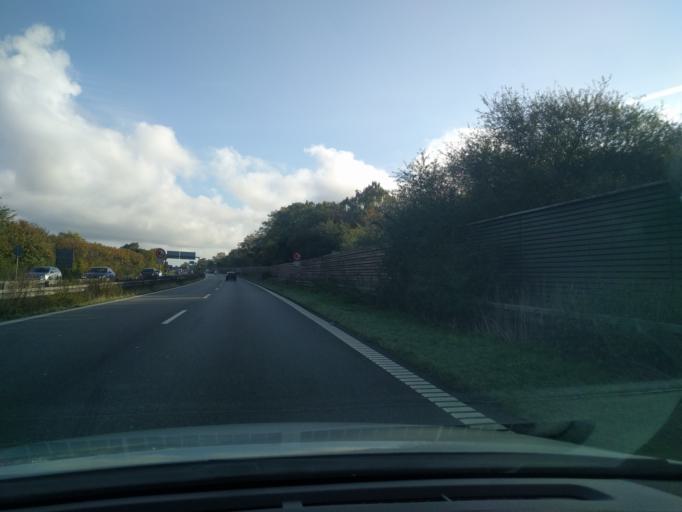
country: DK
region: Zealand
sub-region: Slagelse Kommune
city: Korsor
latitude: 55.3500
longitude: 11.1310
